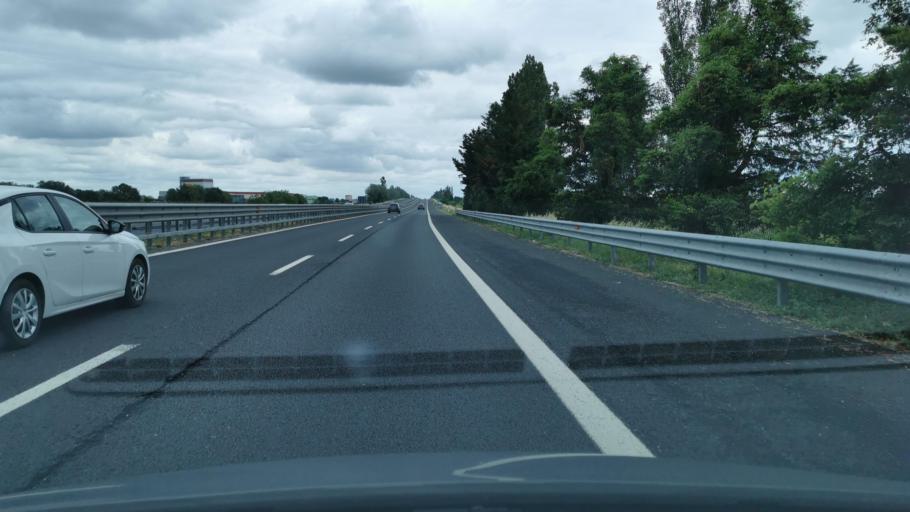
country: IT
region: Emilia-Romagna
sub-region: Provincia di Ravenna
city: Bagnacavallo
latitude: 44.4044
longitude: 11.9783
